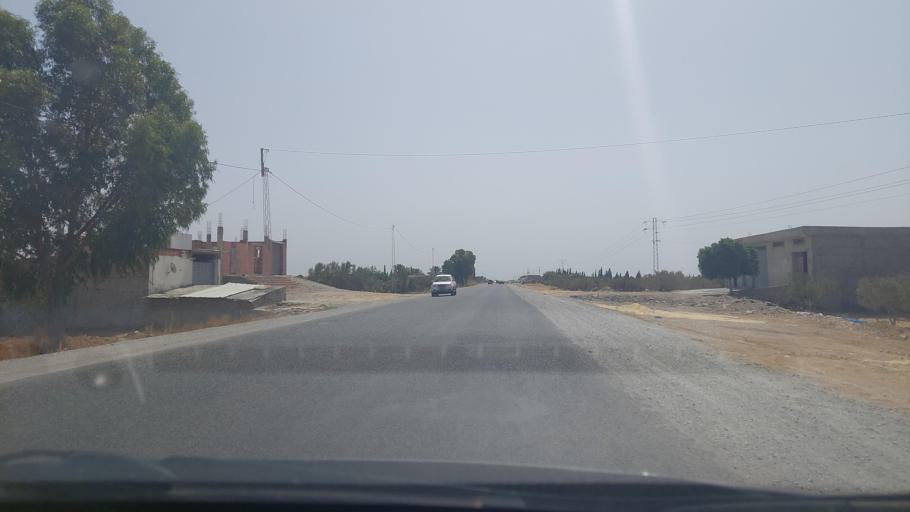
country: TN
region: Al Munastir
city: Qasr Hallal
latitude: 35.6268
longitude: 10.8723
